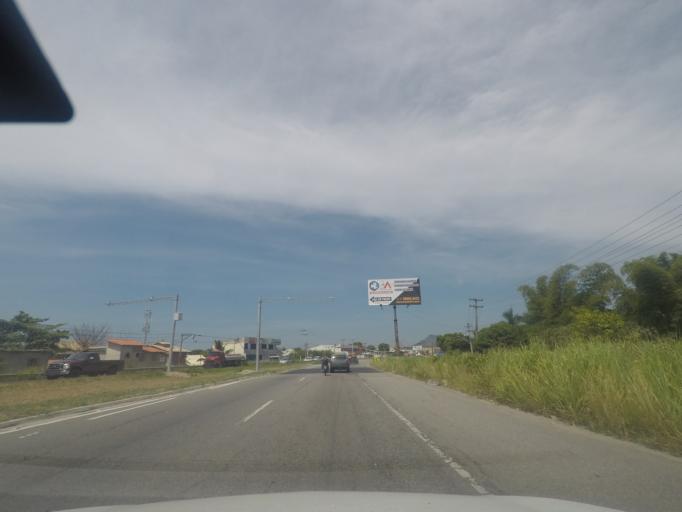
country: BR
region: Rio de Janeiro
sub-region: Marica
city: Marica
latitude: -22.9068
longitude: -42.8185
